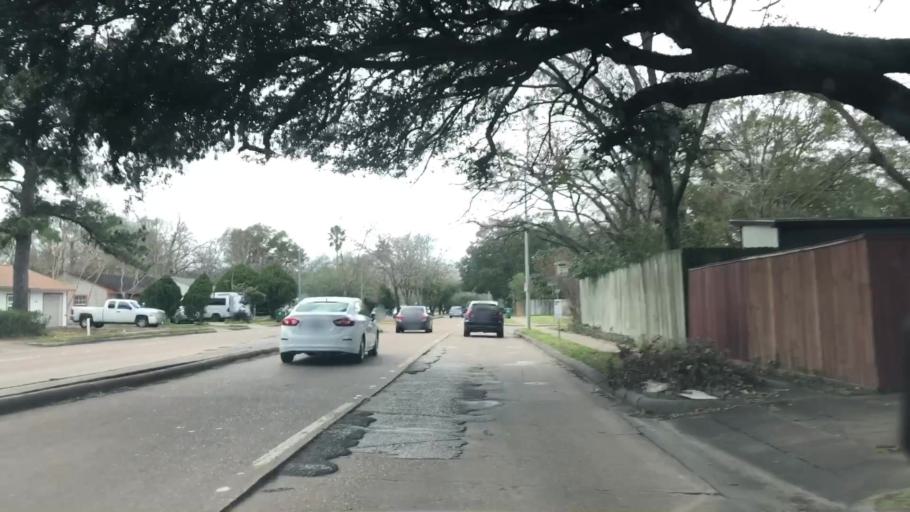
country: US
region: Texas
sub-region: Harris County
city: Bellaire
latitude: 29.6884
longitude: -95.4946
